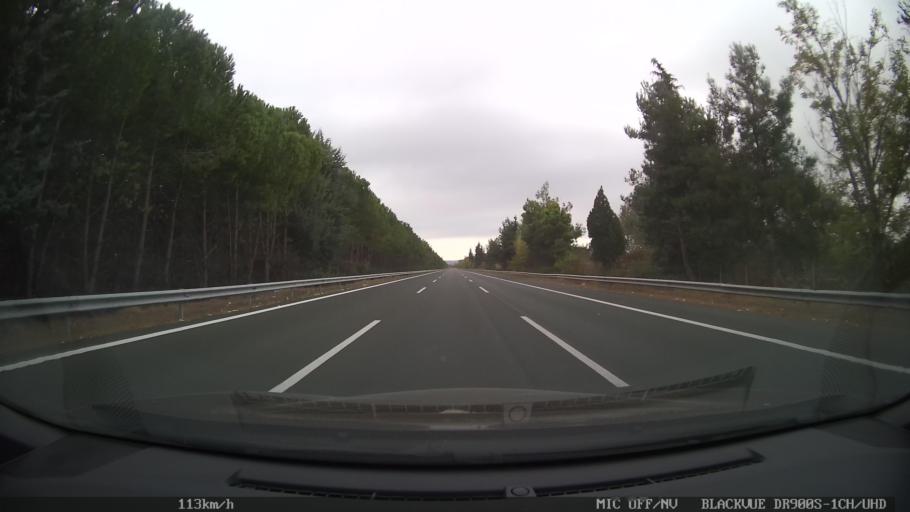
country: GR
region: Central Macedonia
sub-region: Nomos Pierias
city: Aiginio
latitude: 40.5059
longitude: 22.5676
